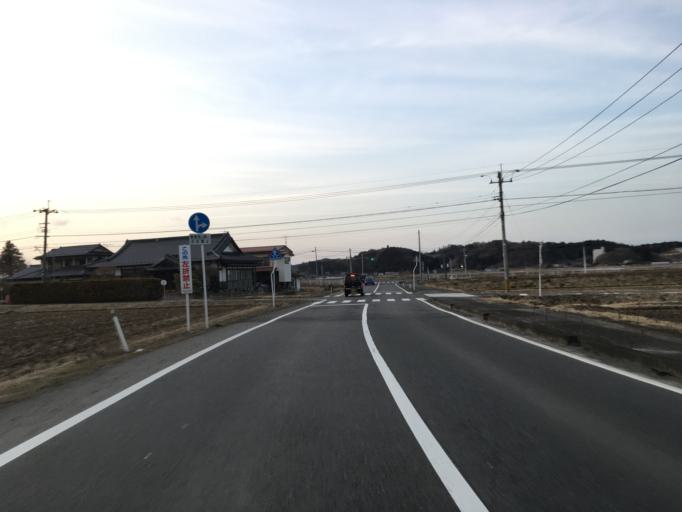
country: JP
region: Fukushima
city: Ishikawa
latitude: 37.0556
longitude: 140.3321
